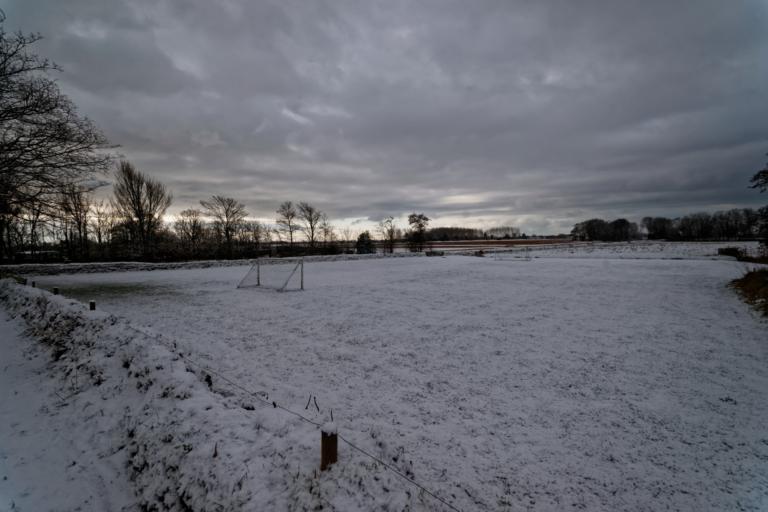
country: NL
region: North Holland
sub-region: Gemeente Texel
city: Den Burg
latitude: 53.0721
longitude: 4.8211
